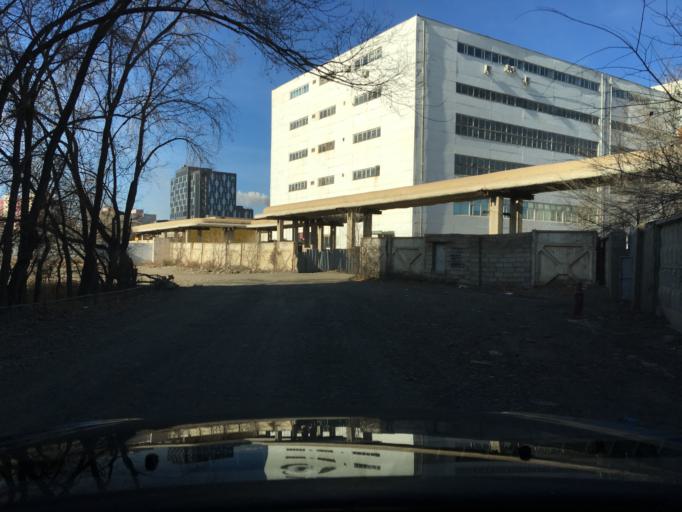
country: MN
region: Ulaanbaatar
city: Ulaanbaatar
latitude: 47.8955
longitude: 106.8887
